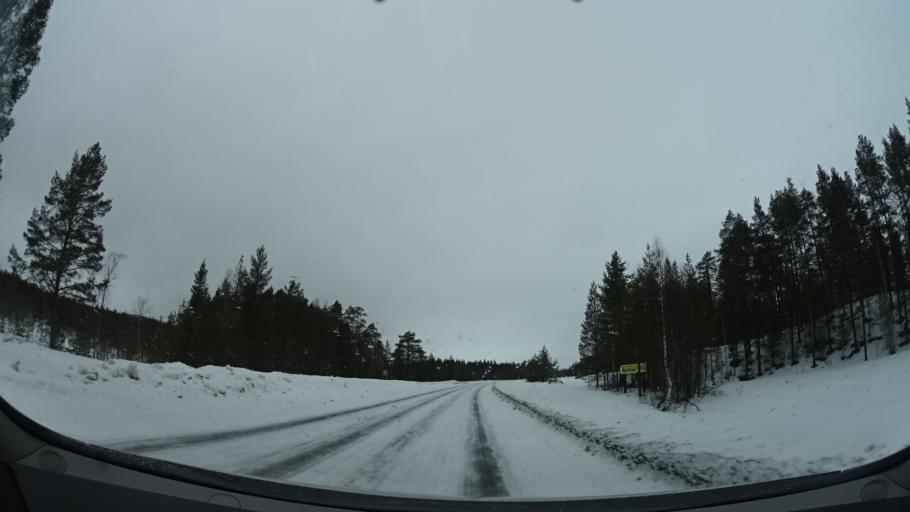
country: SE
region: Vaesterbotten
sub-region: Mala Kommun
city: Mala
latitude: 65.1565
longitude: 18.7909
